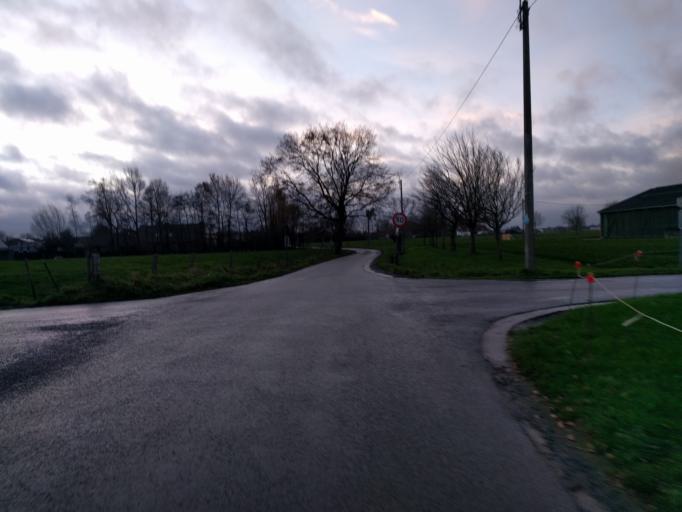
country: BE
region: Flanders
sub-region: Provincie West-Vlaanderen
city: Wevelgem
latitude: 50.8229
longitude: 3.1624
